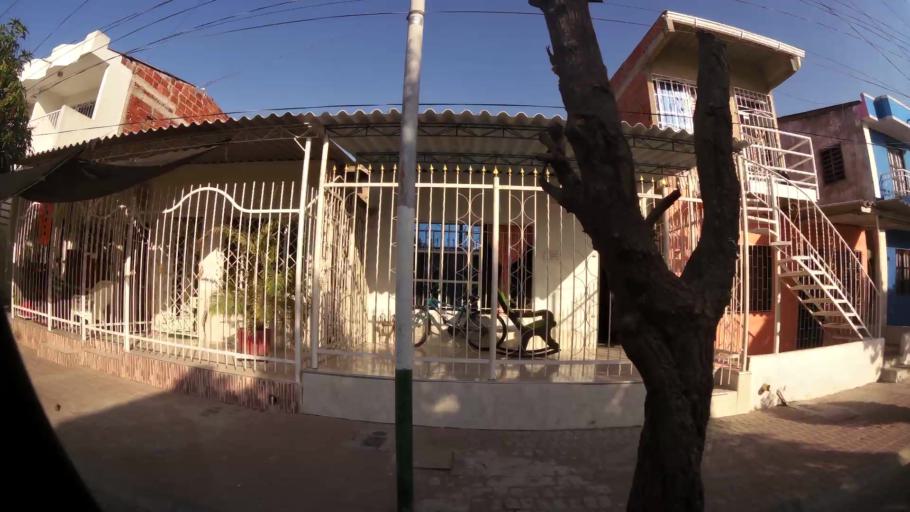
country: CO
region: Bolivar
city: Cartagena
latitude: 10.4124
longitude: -75.4960
